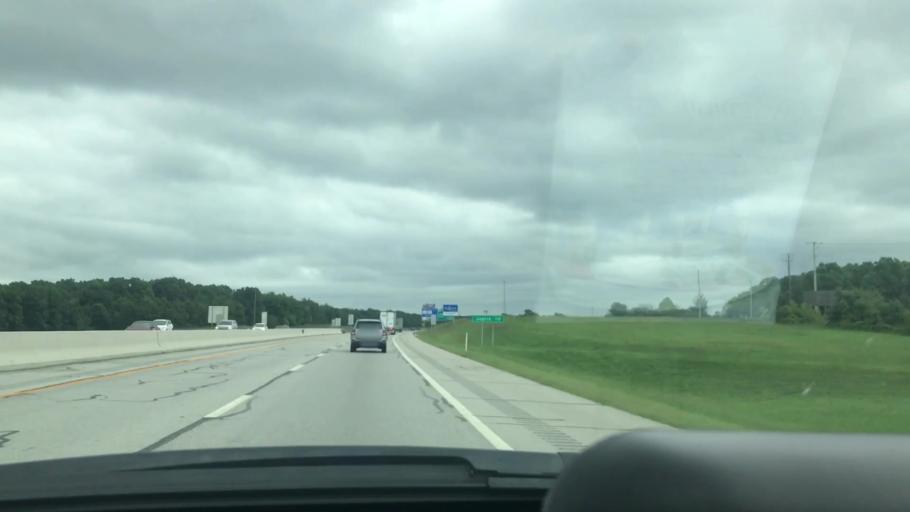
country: US
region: Kansas
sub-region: Cherokee County
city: Galena
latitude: 36.9950
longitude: -94.6198
